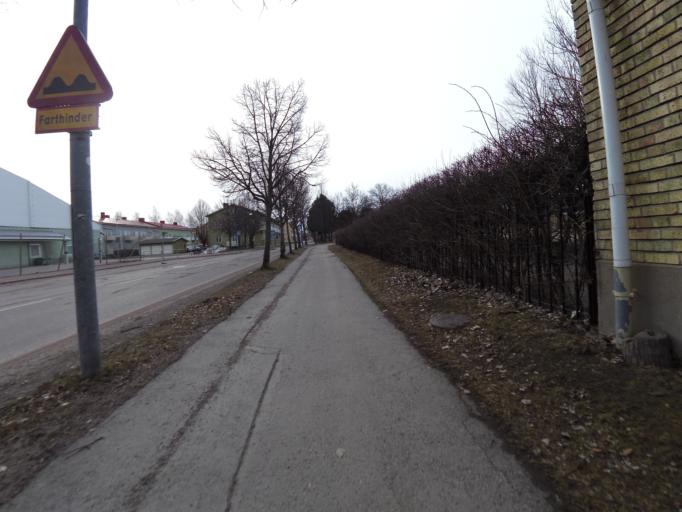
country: SE
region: Gaevleborg
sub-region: Gavle Kommun
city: Gavle
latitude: 60.6788
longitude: 17.1327
